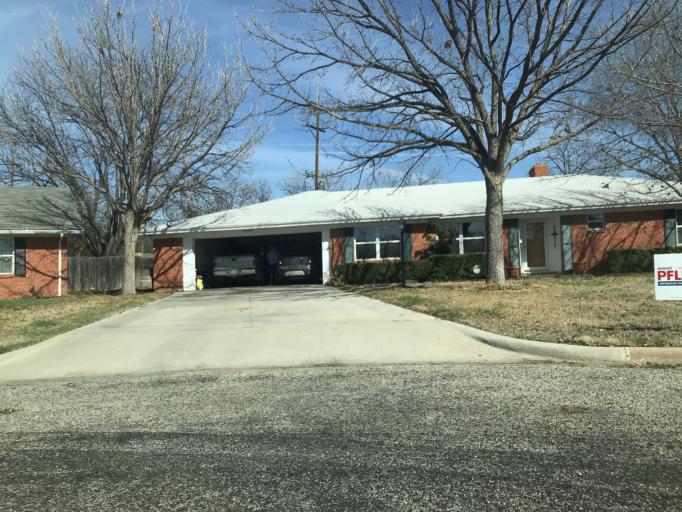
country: US
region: Texas
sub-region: Tom Green County
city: San Angelo
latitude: 31.4393
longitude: -100.4766
